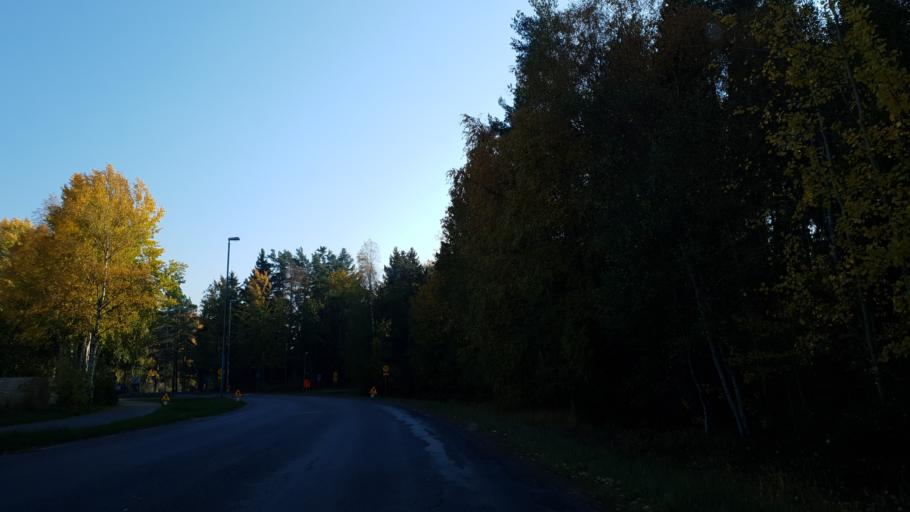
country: SE
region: Stockholm
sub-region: Haninge Kommun
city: Haninge
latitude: 59.1722
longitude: 18.1879
